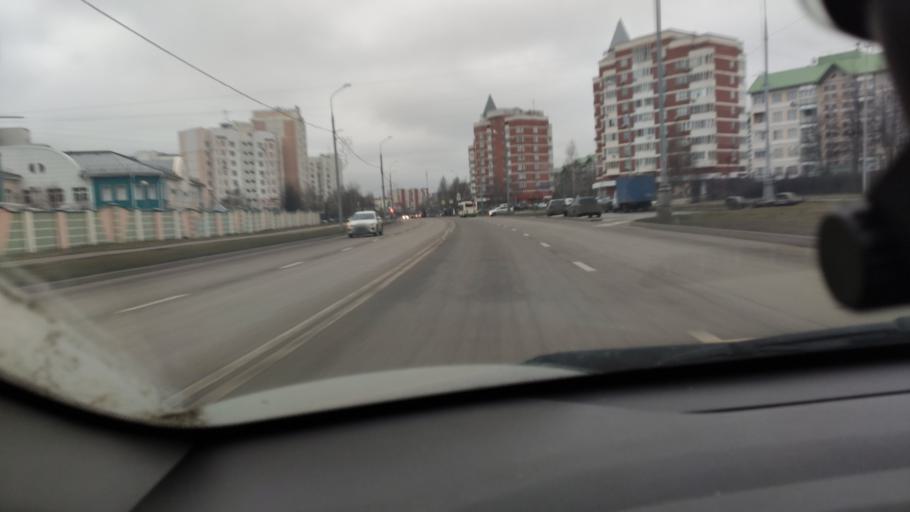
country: RU
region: Moskovskaya
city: Shcherbinka
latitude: 55.5420
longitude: 37.5383
